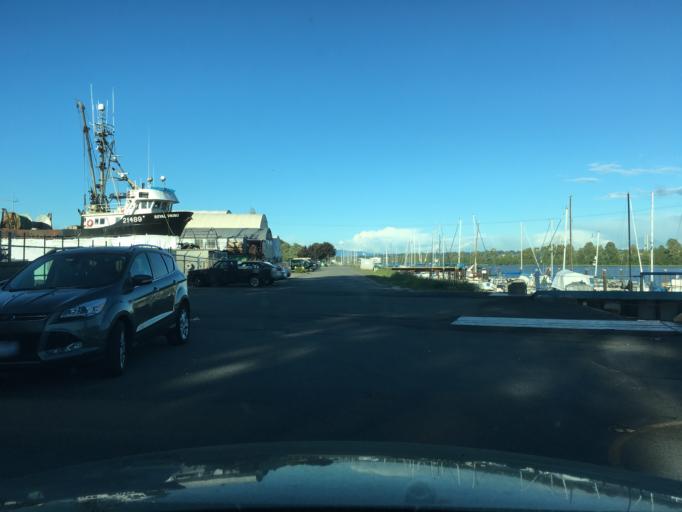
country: CA
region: British Columbia
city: Delta
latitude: 49.1627
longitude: -122.9927
